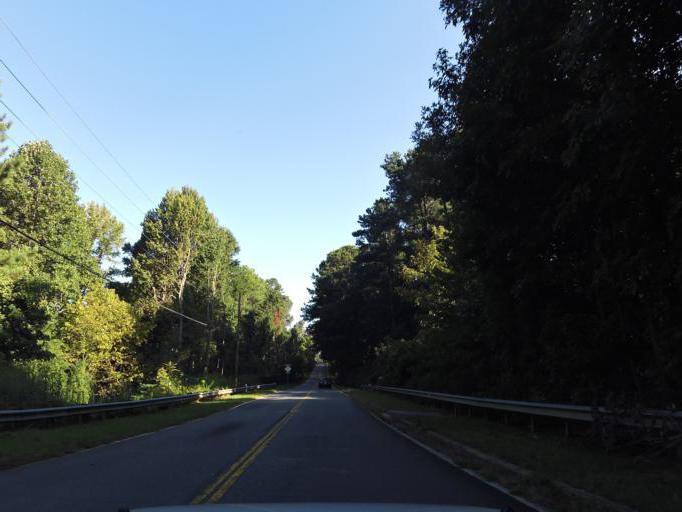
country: US
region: Georgia
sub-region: Cobb County
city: Kennesaw
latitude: 33.9789
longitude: -84.6171
